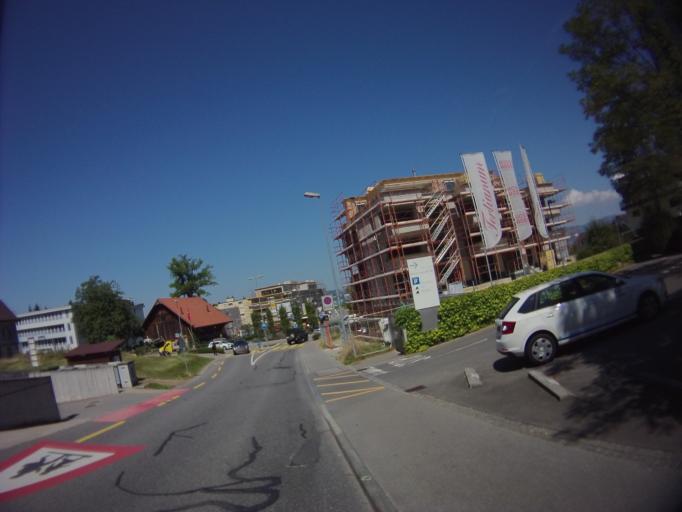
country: CH
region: Schwyz
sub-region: Bezirk Hoefe
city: Freienbach
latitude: 47.2007
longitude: 8.7810
